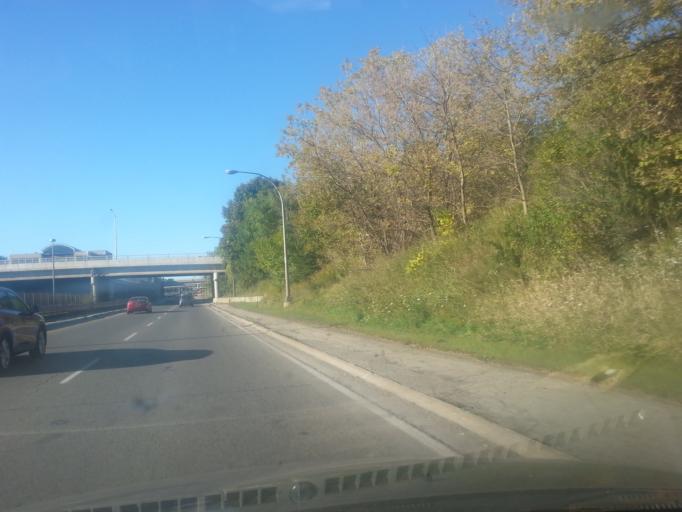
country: CA
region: Ontario
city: Toronto
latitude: 43.7071
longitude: -79.4394
